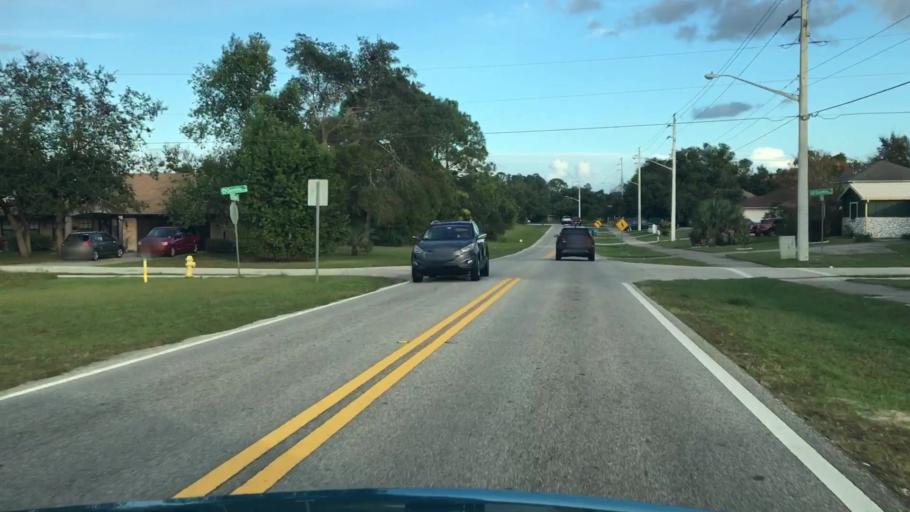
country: US
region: Florida
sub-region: Volusia County
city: Deltona
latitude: 28.9206
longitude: -81.2008
